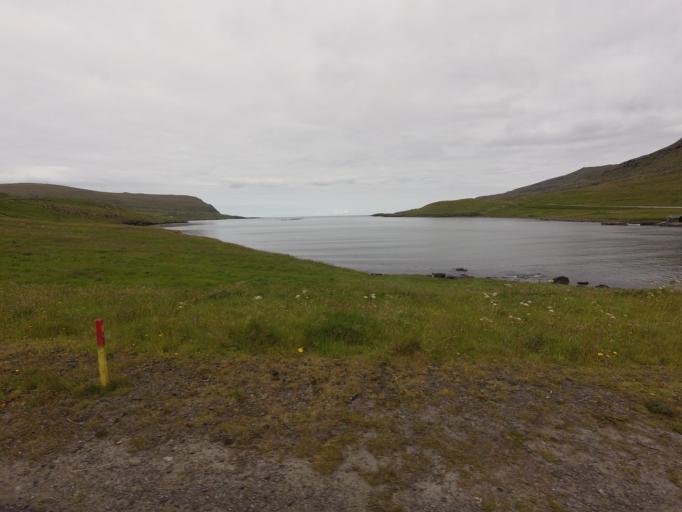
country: FO
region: Suduroy
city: Tvoroyri
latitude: 61.5352
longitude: -6.8121
